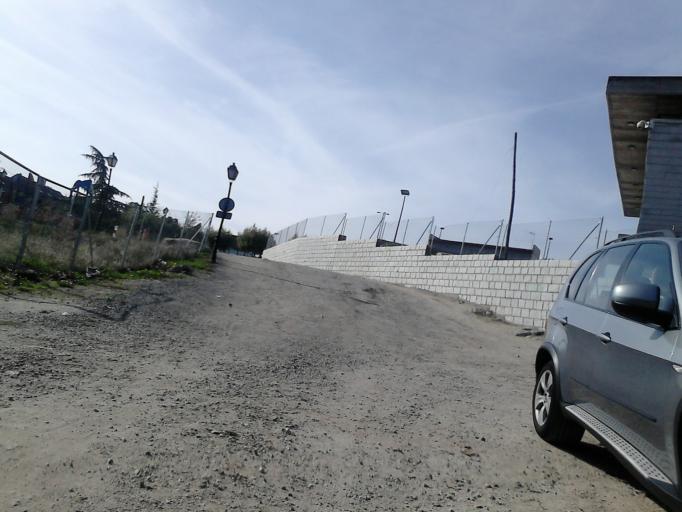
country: ES
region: Madrid
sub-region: Provincia de Madrid
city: Galapagar
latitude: 40.5830
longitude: -4.0080
